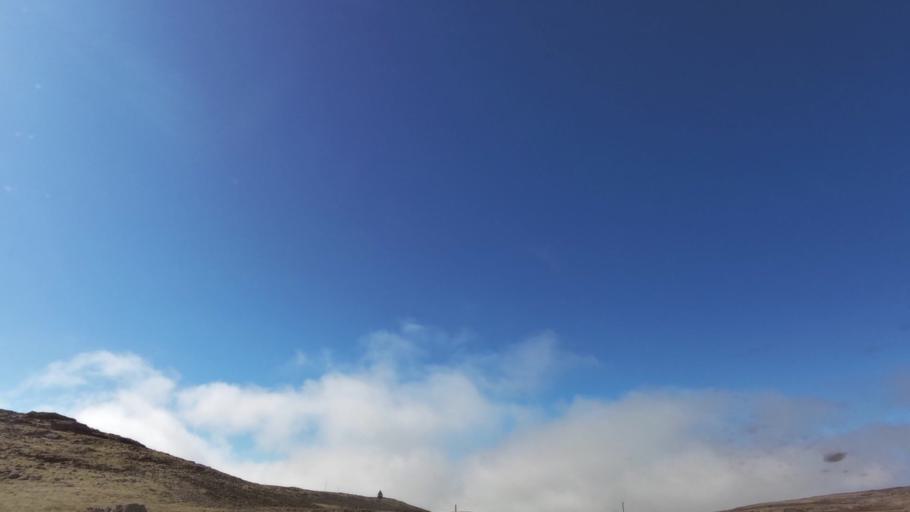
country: IS
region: West
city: Olafsvik
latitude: 65.5524
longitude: -24.2196
